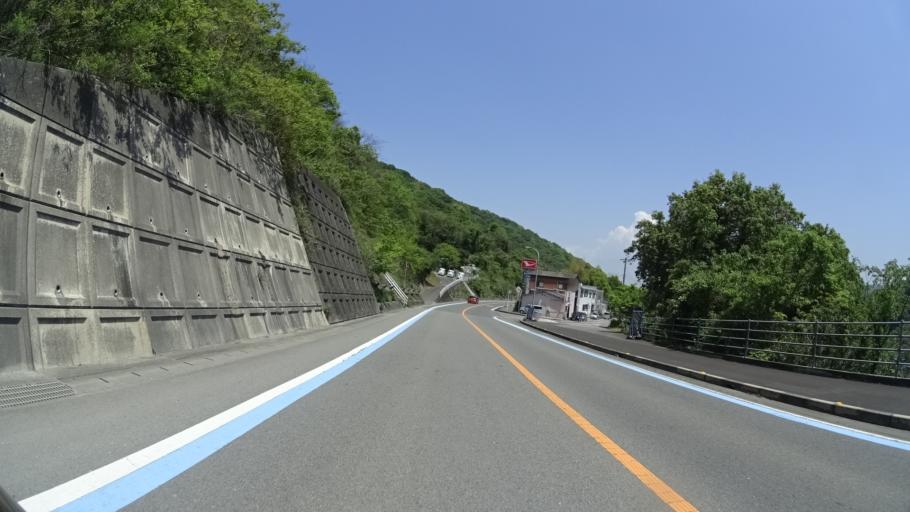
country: JP
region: Ehime
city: Iyo
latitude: 33.7257
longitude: 132.6840
